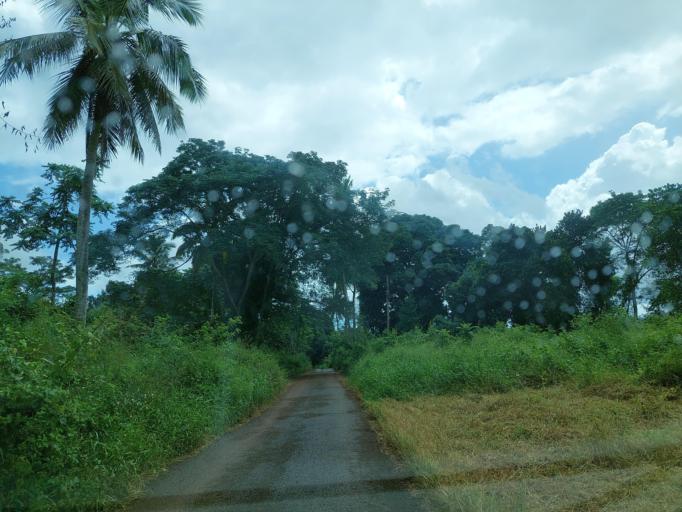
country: YT
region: M'Tsangamouji
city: M'Tsangamouji
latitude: -12.7530
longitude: 45.1221
